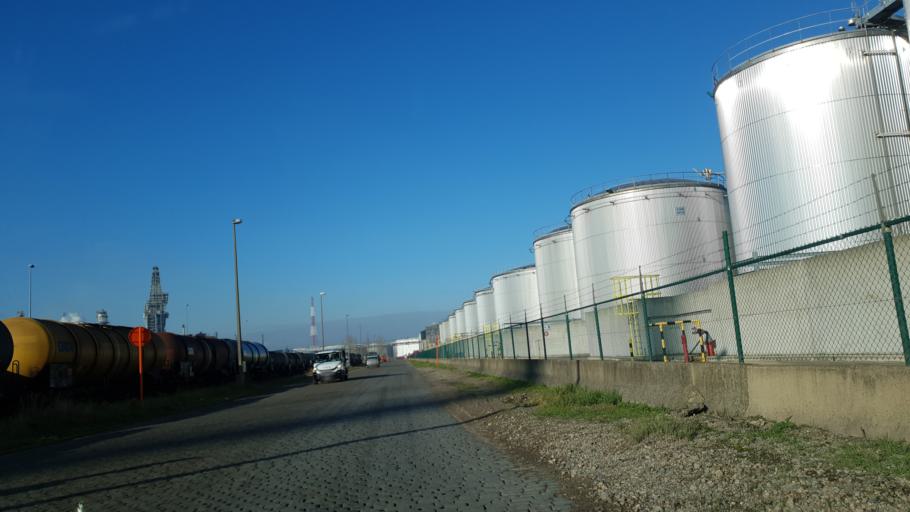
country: BE
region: Flanders
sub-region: Provincie Antwerpen
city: Zwijndrecht
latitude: 51.2615
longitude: 4.3460
